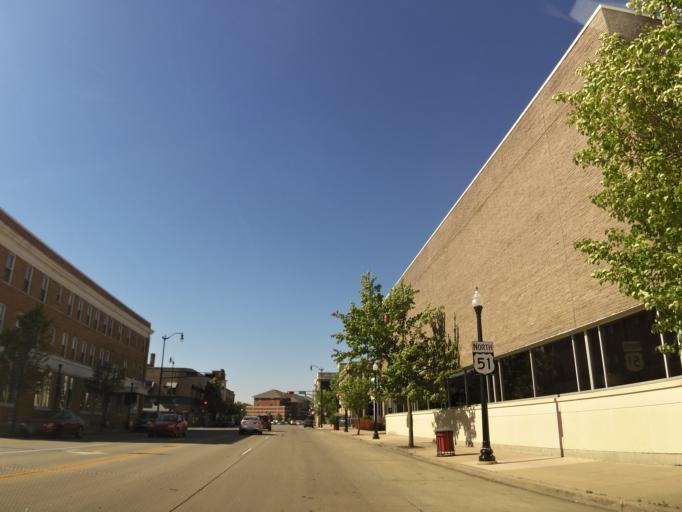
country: US
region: Illinois
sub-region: Winnebago County
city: South Beloit
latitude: 42.4989
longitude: -89.0337
